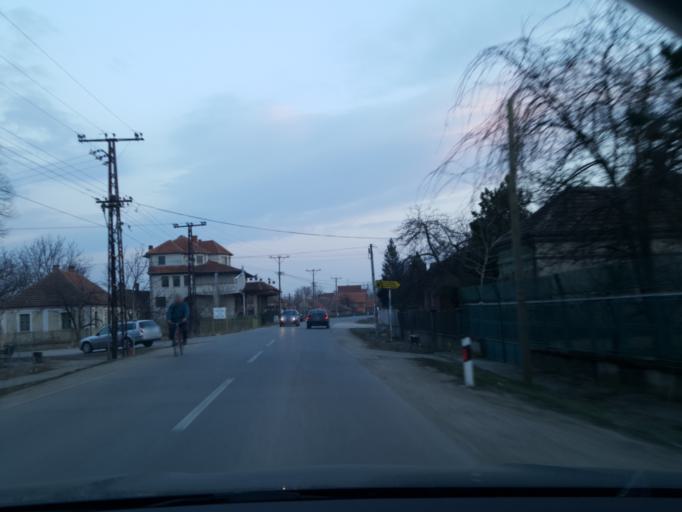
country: RS
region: Central Serbia
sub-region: Nisavski Okrug
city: Aleksinac
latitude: 43.5007
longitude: 21.7031
